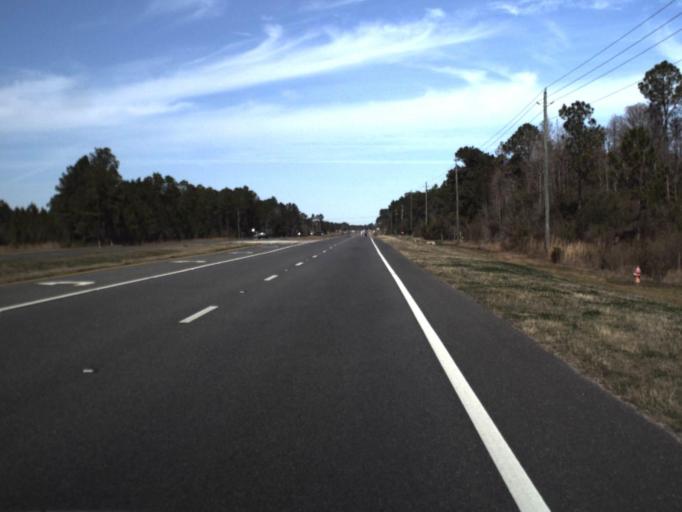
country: US
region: Florida
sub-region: Bay County
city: Lynn Haven
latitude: 30.3582
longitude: -85.6684
